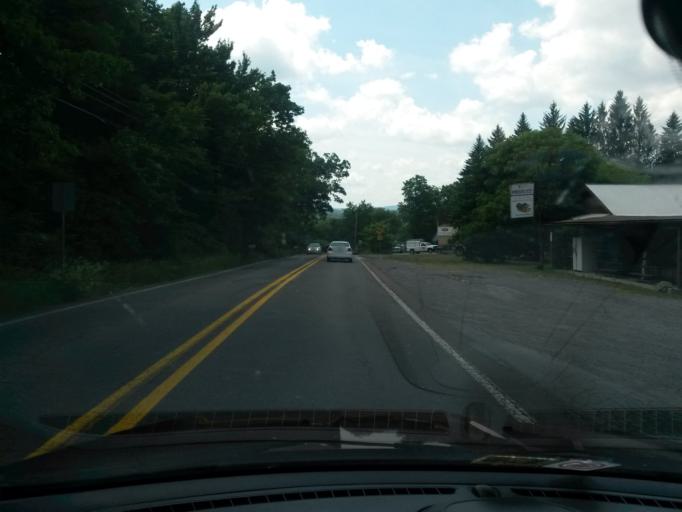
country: US
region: West Virginia
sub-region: Mercer County
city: Princeton
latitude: 37.3703
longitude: -81.1099
